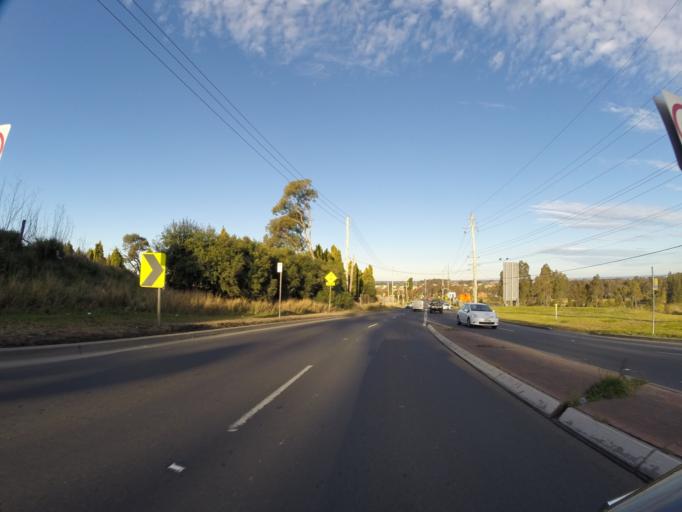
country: AU
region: New South Wales
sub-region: Fairfield
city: Horsley Park
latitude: -33.8455
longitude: 150.8716
